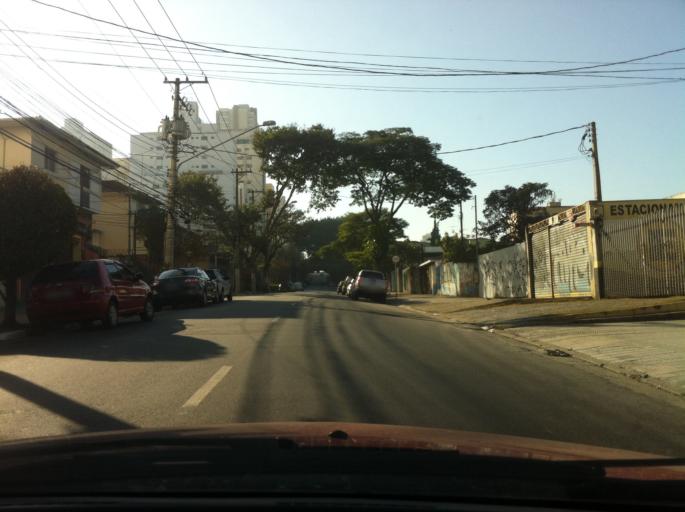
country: BR
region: Sao Paulo
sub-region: Sao Paulo
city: Sao Paulo
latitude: -23.6039
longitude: -46.6482
